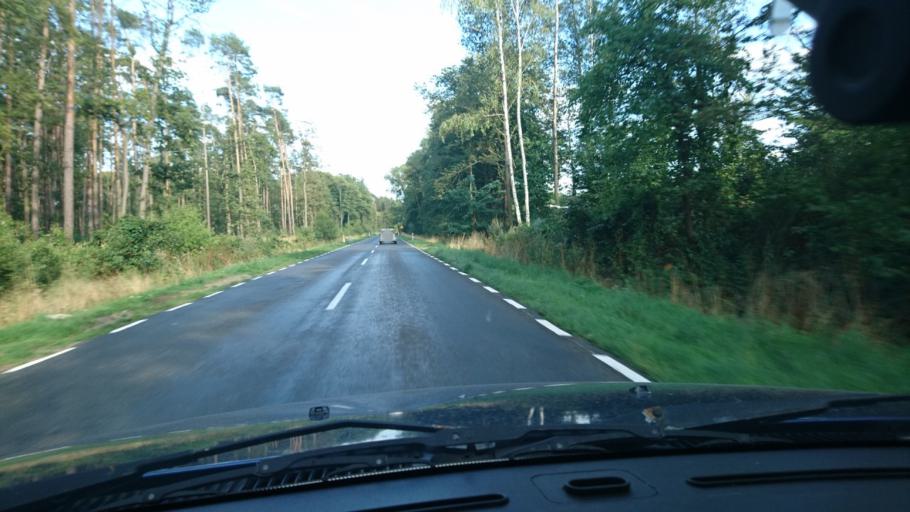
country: PL
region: Greater Poland Voivodeship
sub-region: Powiat krotoszynski
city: Sulmierzyce
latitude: 51.6023
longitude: 17.5838
